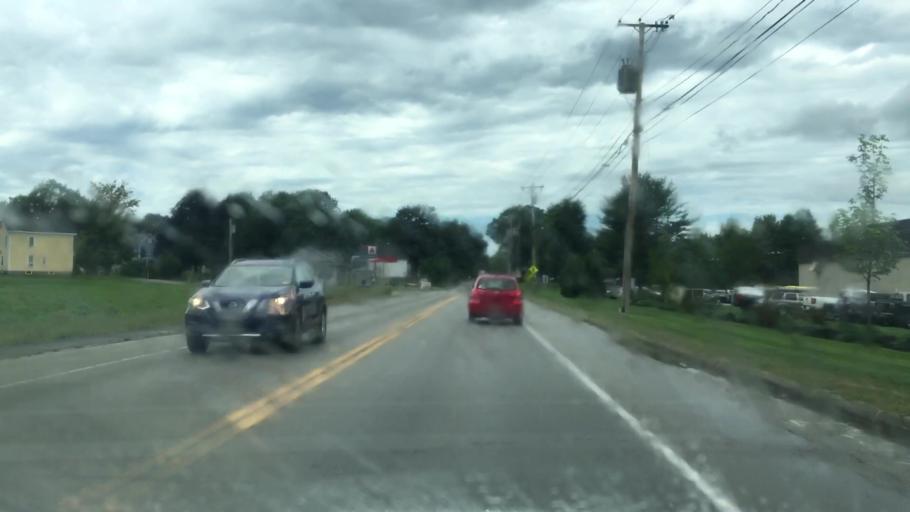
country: US
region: Maine
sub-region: York County
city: North Berwick
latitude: 43.3080
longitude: -70.7263
